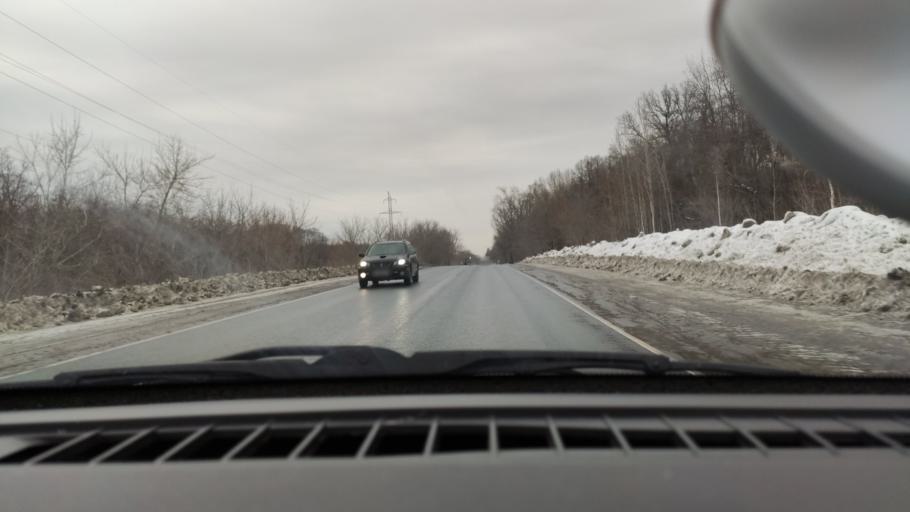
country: RU
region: Samara
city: Petra-Dubrava
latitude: 53.3183
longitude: 50.2685
